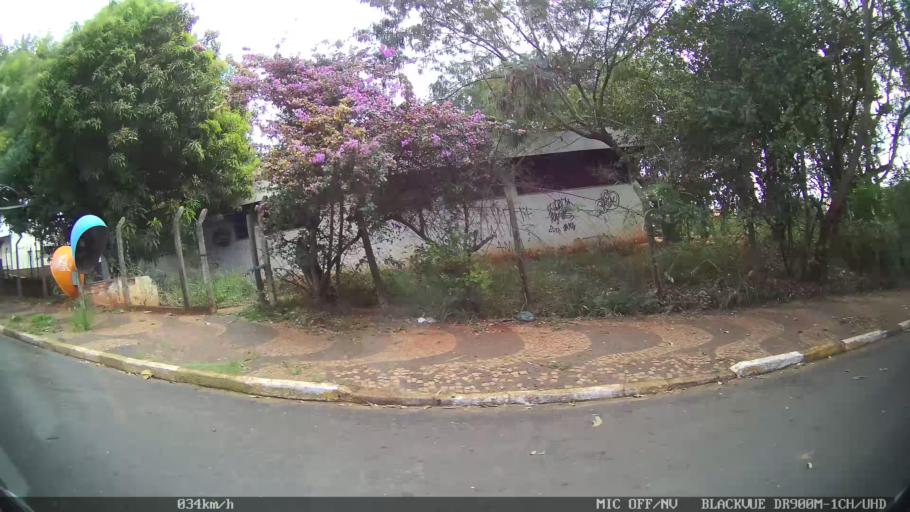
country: BR
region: Sao Paulo
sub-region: Paulinia
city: Paulinia
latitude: -22.7510
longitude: -47.1738
